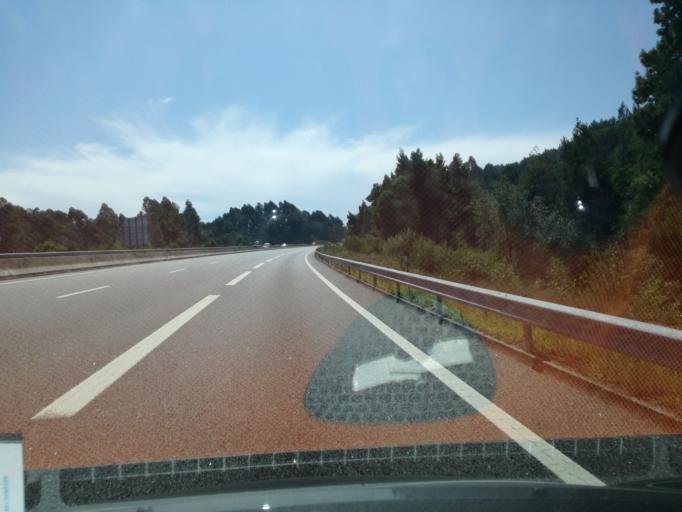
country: PT
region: Viana do Castelo
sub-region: Caminha
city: Vila Praia de Ancora
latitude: 41.7954
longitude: -8.7935
